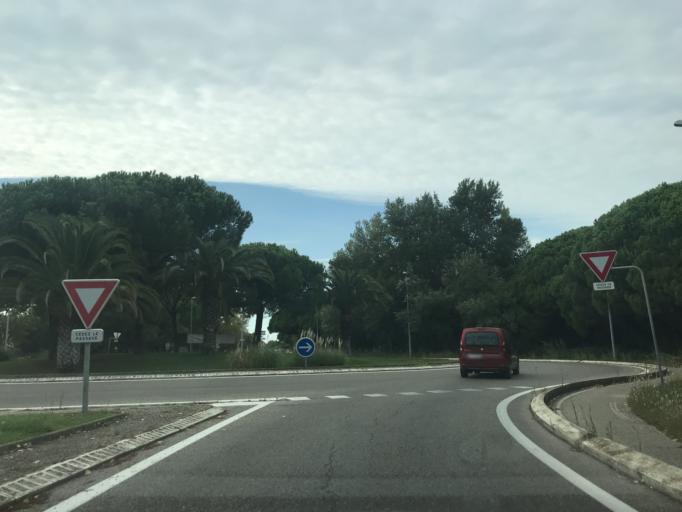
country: FR
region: Languedoc-Roussillon
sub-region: Departement du Gard
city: Le Grau-du-Roi
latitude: 43.5510
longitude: 4.1185
